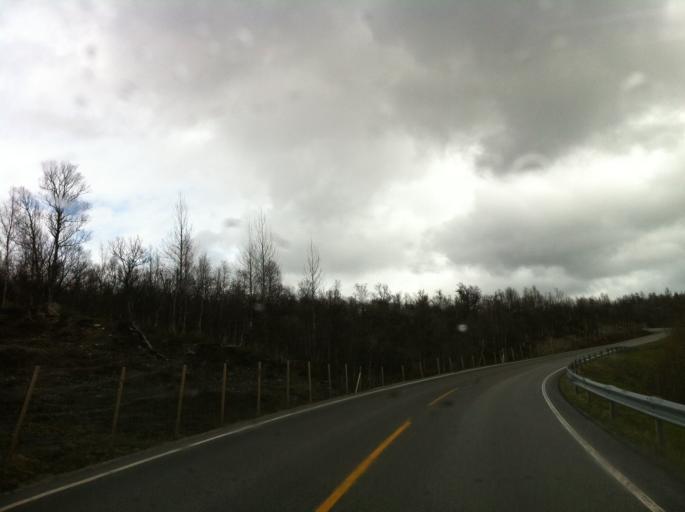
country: NO
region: Sor-Trondelag
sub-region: Tydal
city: Aas
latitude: 62.6467
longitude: 11.8727
